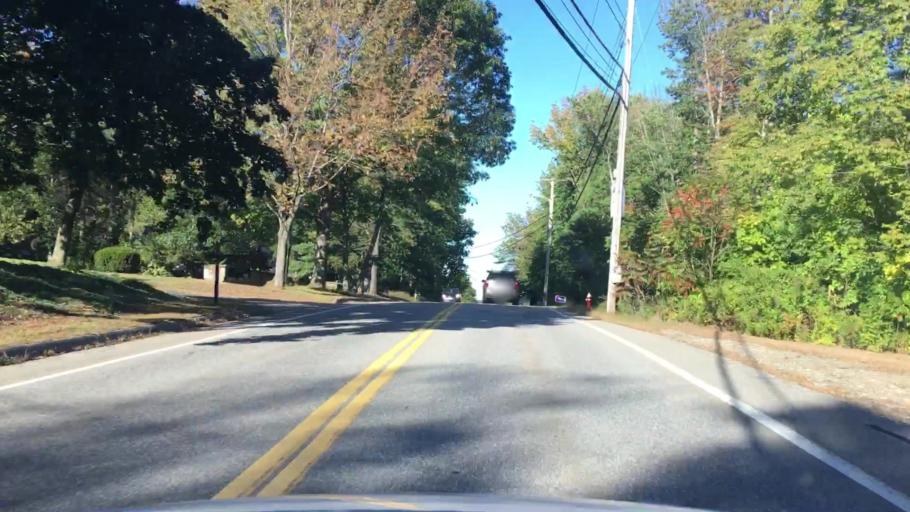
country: US
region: Maine
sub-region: Androscoggin County
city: Lewiston
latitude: 44.0870
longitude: -70.1662
